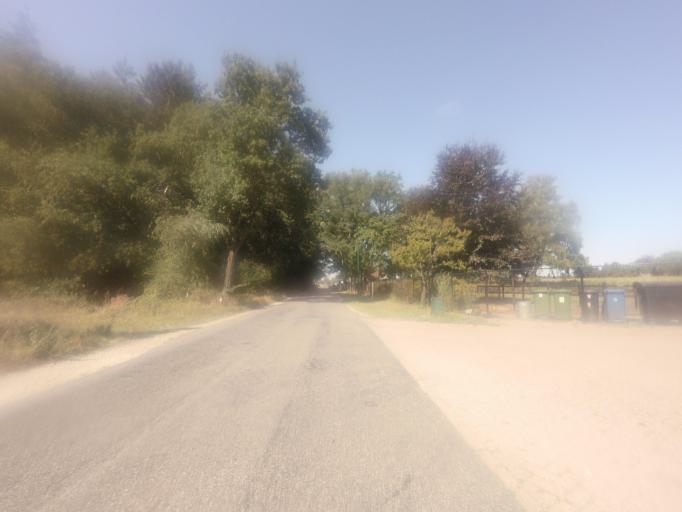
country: NL
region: North Brabant
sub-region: Gemeente Veldhoven
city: Oerle
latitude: 51.3971
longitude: 5.3839
